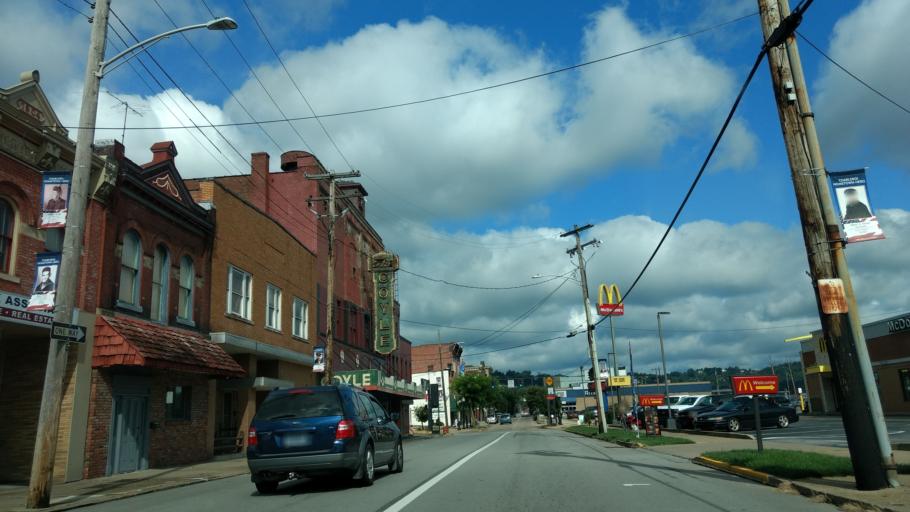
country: US
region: Pennsylvania
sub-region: Washington County
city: Charleroi
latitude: 40.1369
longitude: -79.8959
